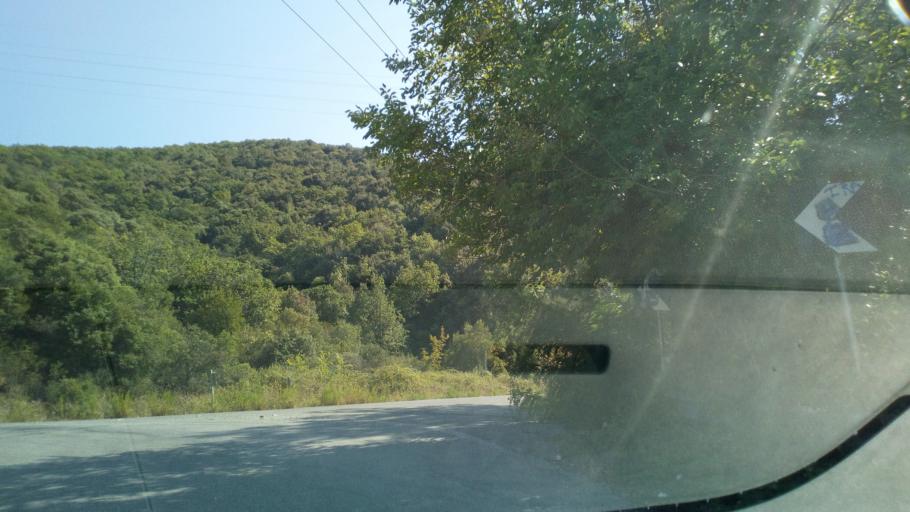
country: GR
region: Central Macedonia
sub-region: Nomos Thessalonikis
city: Stavros
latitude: 40.6554
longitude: 23.7328
